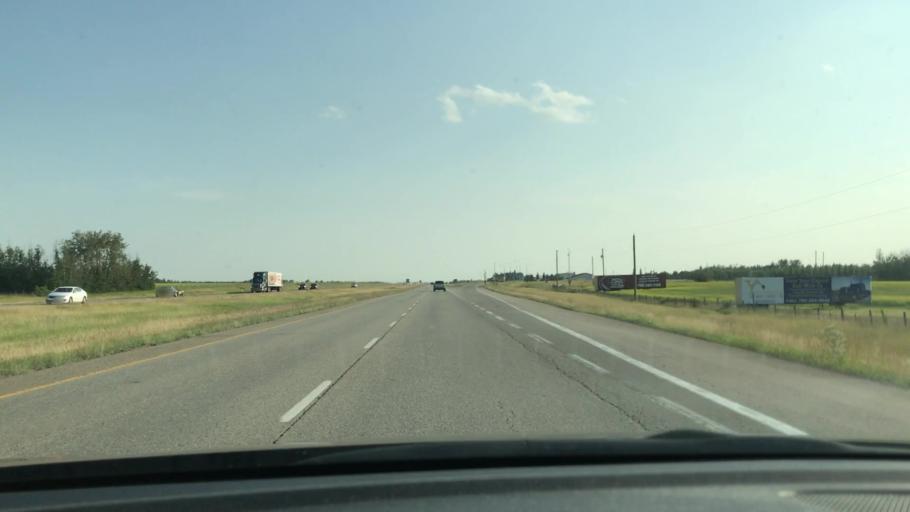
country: CA
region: Alberta
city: Leduc
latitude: 53.2377
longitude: -113.5664
